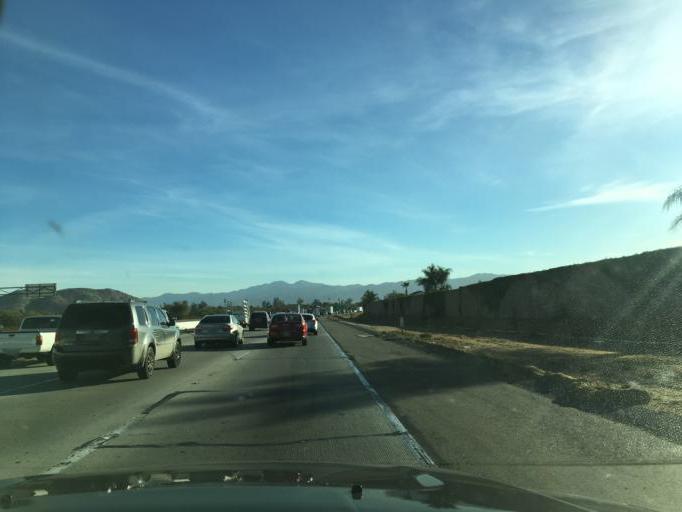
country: US
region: California
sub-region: Riverside County
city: Norco
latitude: 33.9598
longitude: -117.5491
